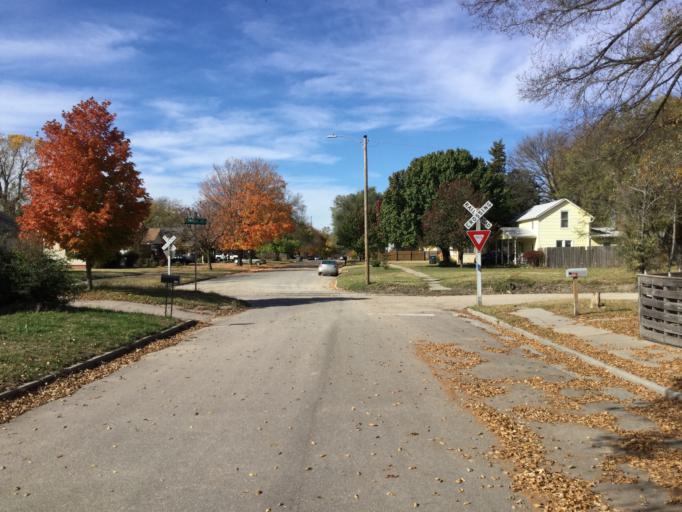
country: US
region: Kansas
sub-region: Harvey County
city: Newton
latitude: 38.0547
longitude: -97.3364
